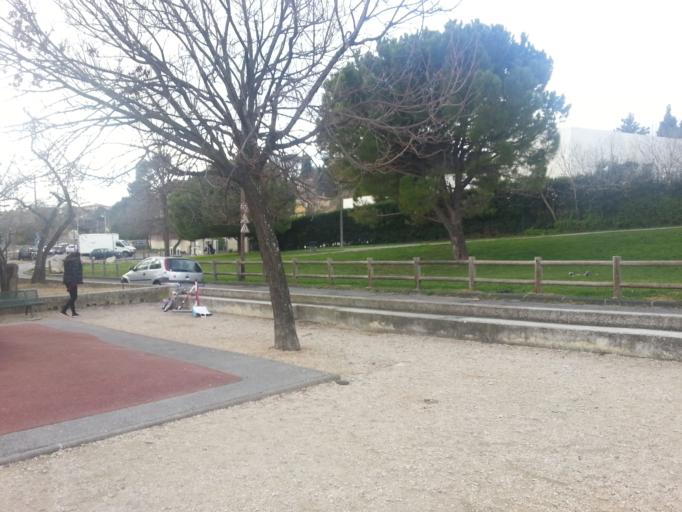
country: FR
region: Provence-Alpes-Cote d'Azur
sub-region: Departement des Bouches-du-Rhone
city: Marseille 04
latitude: 43.3008
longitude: 5.4101
